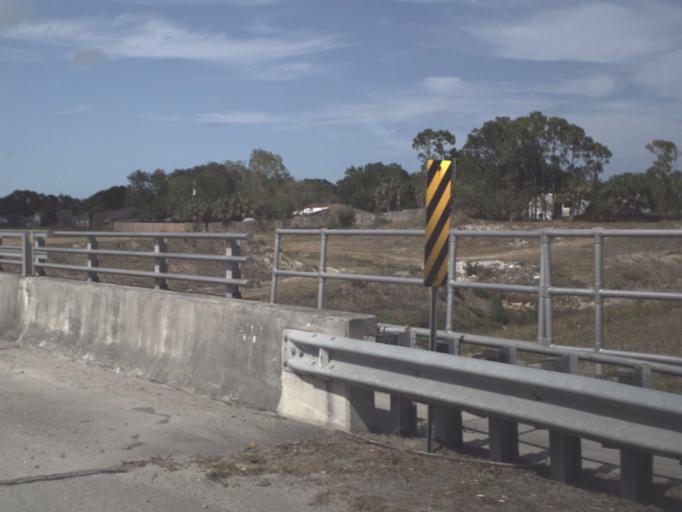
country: US
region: Florida
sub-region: Brevard County
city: June Park
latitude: 28.0133
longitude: -80.6721
